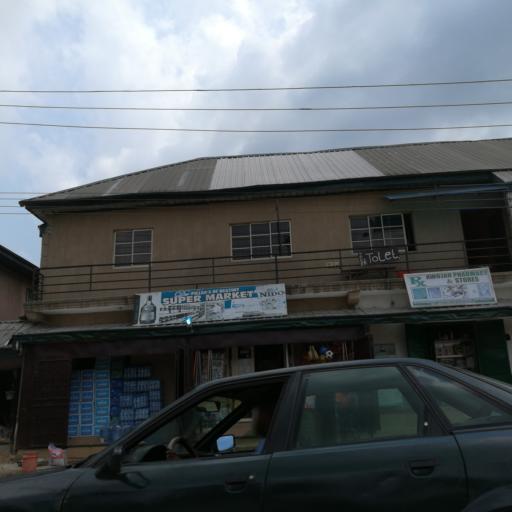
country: NG
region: Rivers
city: Port Harcourt
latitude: 4.8451
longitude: 7.0649
